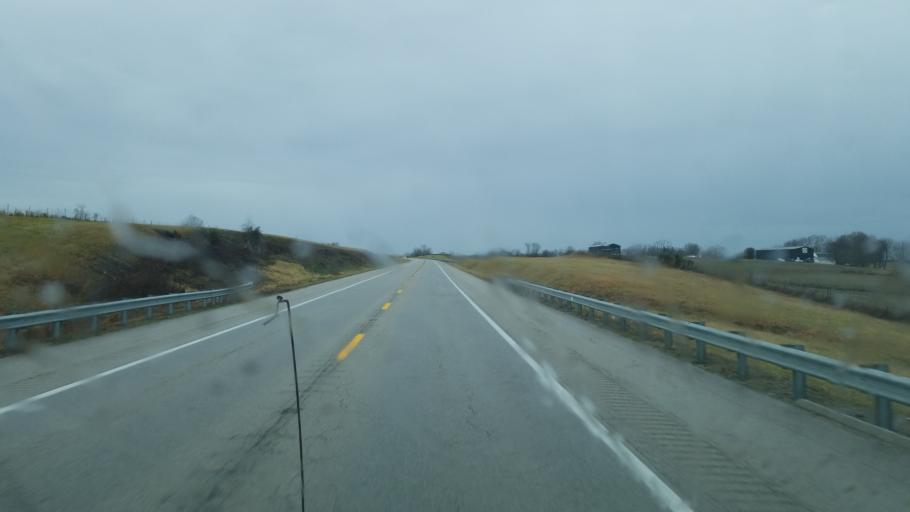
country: US
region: Ohio
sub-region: Adams County
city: Manchester
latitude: 38.5638
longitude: -83.6200
